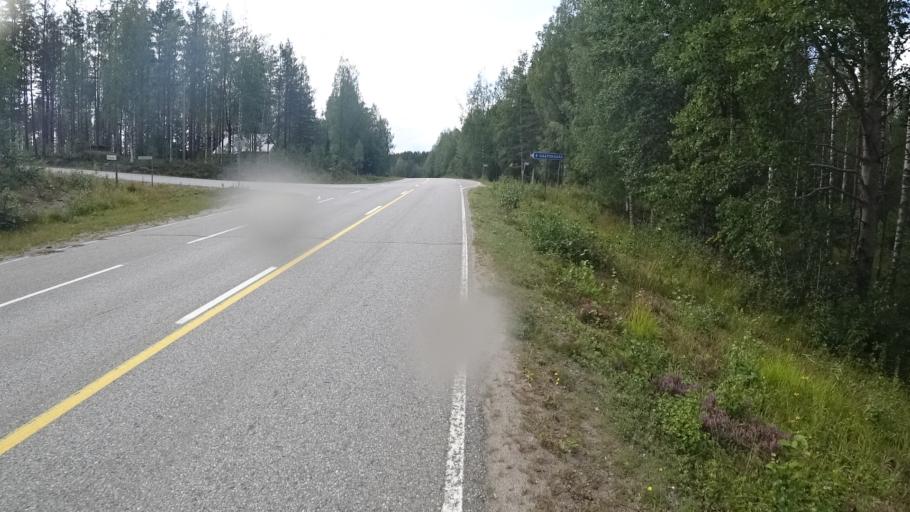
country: FI
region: North Karelia
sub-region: Joensuu
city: Ilomantsi
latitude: 62.6186
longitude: 31.2145
